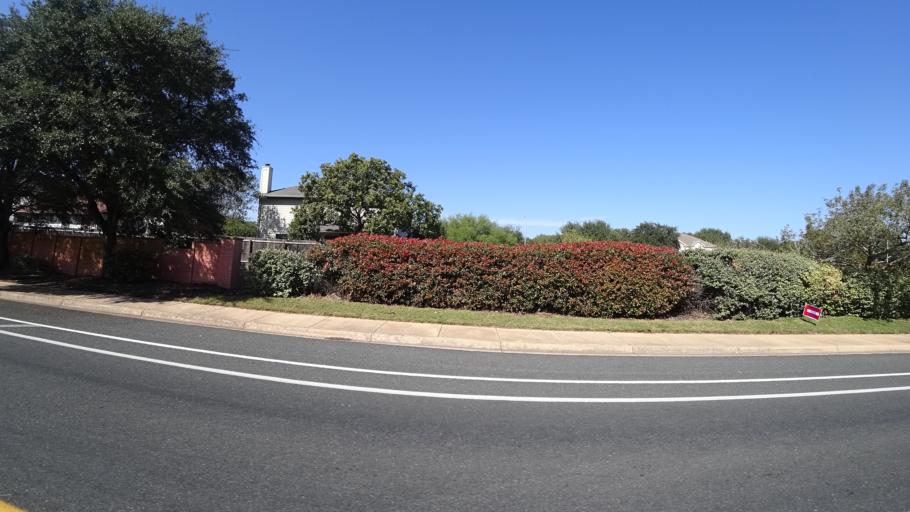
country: US
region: Texas
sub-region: Travis County
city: Shady Hollow
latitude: 30.2183
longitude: -97.8608
